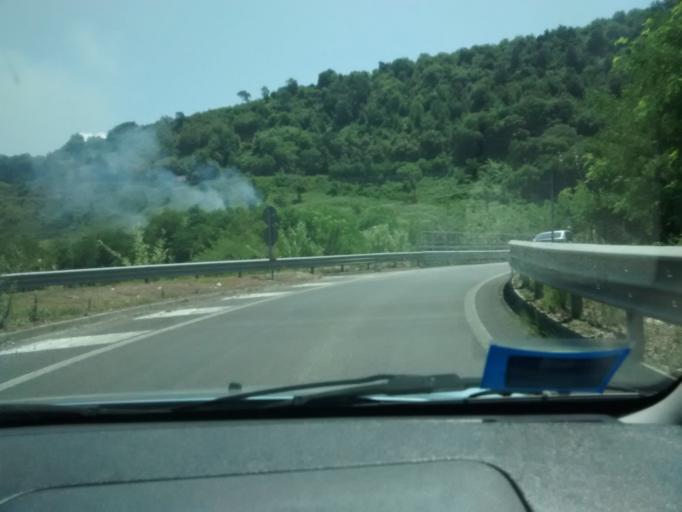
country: IT
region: Calabria
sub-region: Provincia di Catanzaro
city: Maida
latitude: 38.9015
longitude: 16.3886
